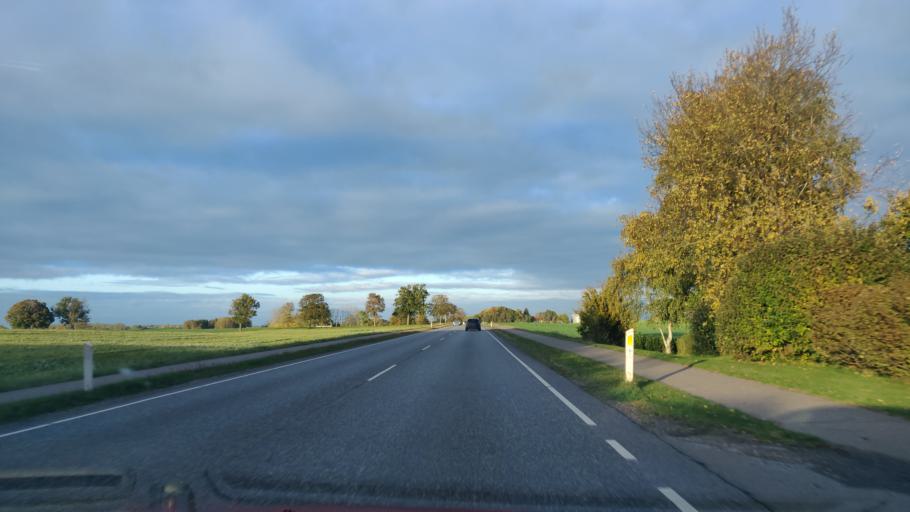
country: DK
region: Zealand
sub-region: Holbaek Kommune
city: Vipperod
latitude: 55.6627
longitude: 11.6822
